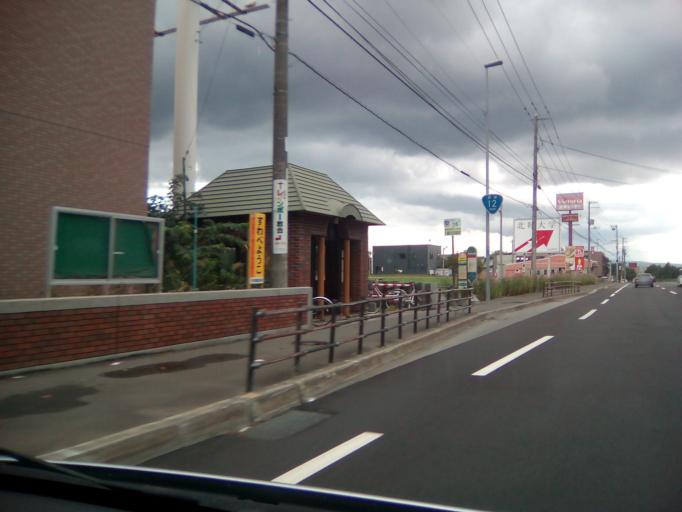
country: JP
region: Hokkaido
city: Ebetsu
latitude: 43.0659
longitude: 141.4887
